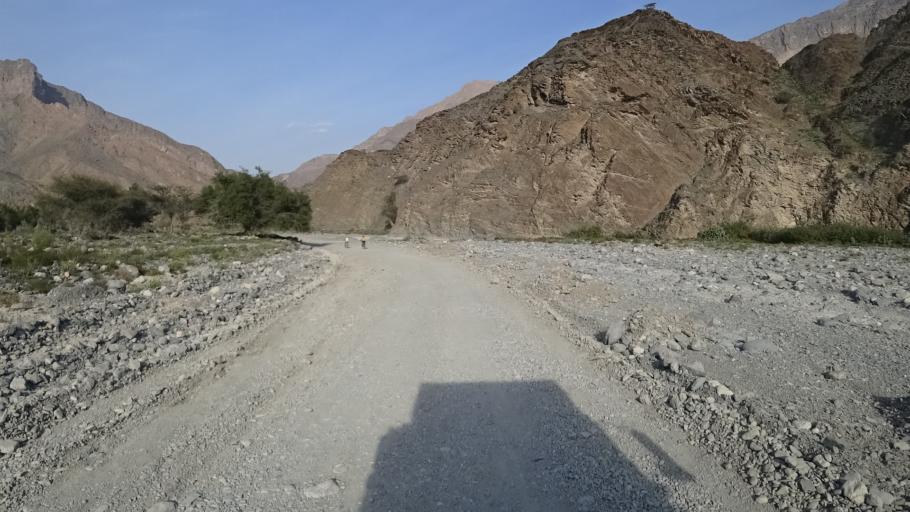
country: OM
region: Al Batinah
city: Bayt al `Awabi
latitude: 23.2634
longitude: 57.4459
